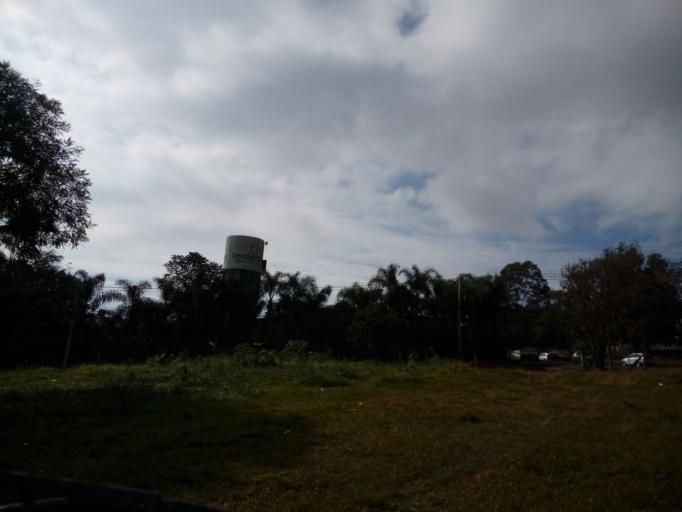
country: BR
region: Santa Catarina
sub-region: Chapeco
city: Chapeco
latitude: -27.1001
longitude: -52.5945
